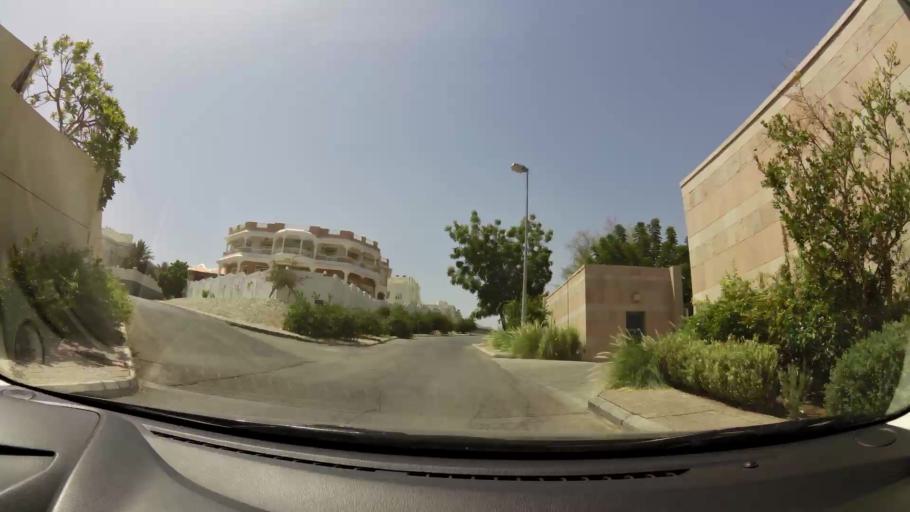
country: OM
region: Muhafazat Masqat
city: Bawshar
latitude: 23.5962
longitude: 58.4543
